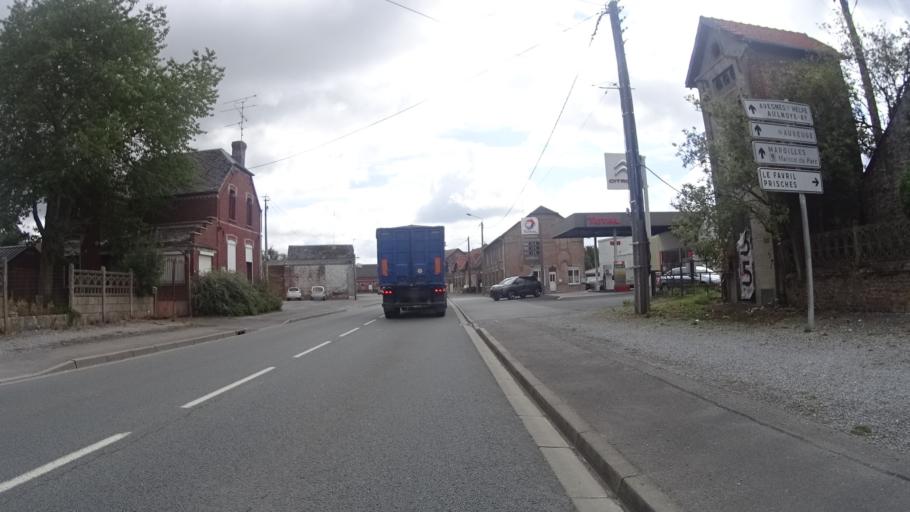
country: FR
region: Nord-Pas-de-Calais
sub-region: Departement du Nord
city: Landrecies
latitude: 50.1186
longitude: 3.7031
